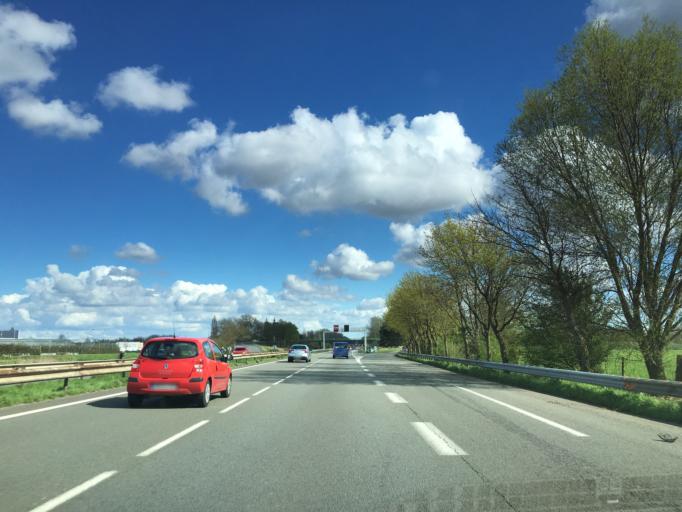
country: FR
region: Nord-Pas-de-Calais
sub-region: Departement du Nord
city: Erquinghem-Lys
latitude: 50.6855
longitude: 2.8362
